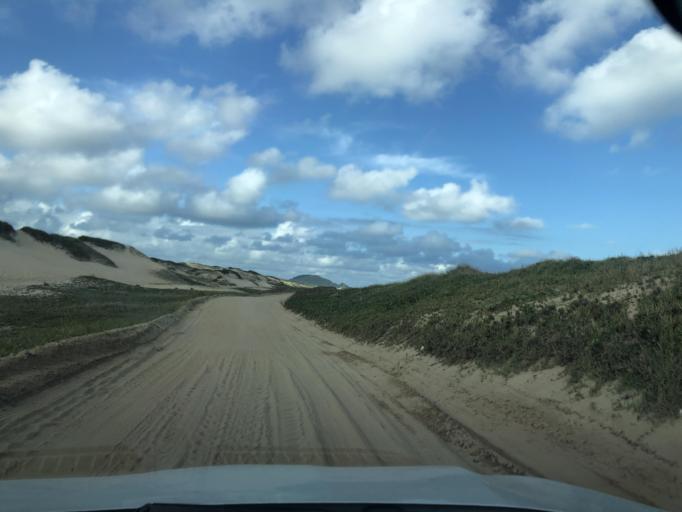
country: BR
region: Santa Catarina
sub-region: Sao Francisco Do Sul
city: Sao Francisco do Sul
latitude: -26.2627
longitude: -48.5204
